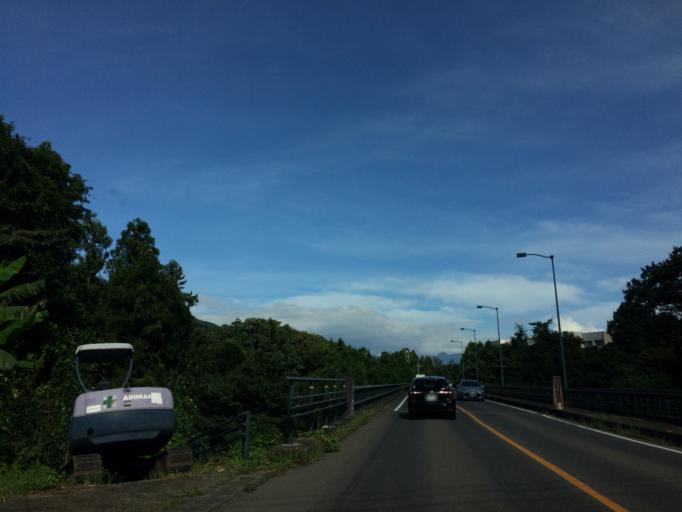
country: JP
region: Gunma
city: Nakanojomachi
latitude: 36.5488
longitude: 138.9166
